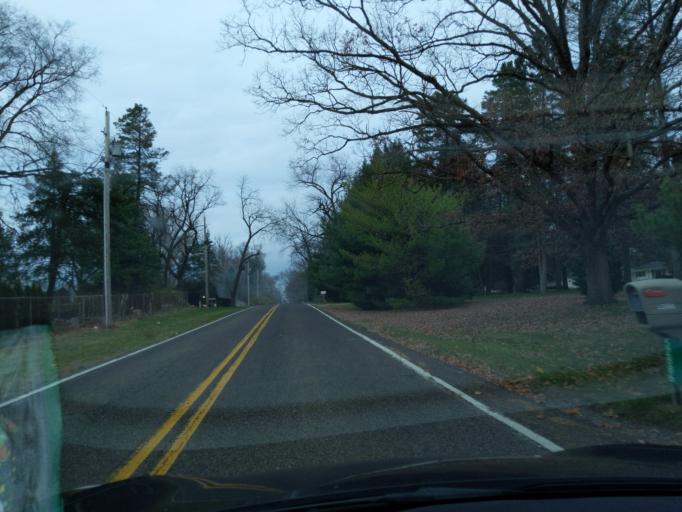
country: US
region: Indiana
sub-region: Saint Joseph County
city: Georgetown
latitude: 41.7252
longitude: -86.2554
